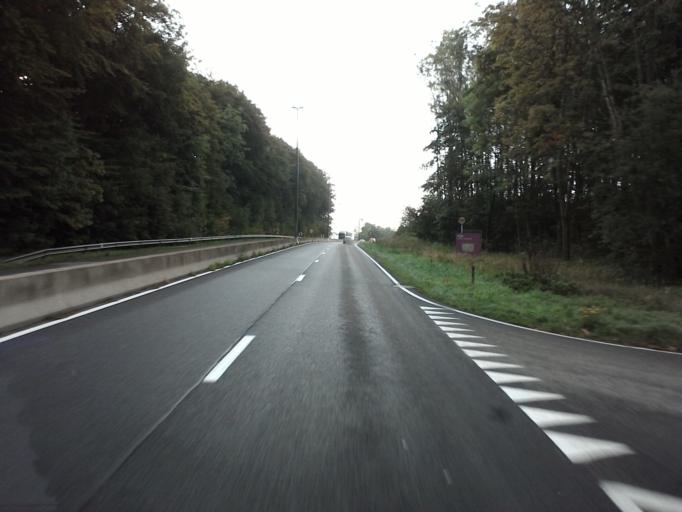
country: BE
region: Wallonia
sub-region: Province du Luxembourg
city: Attert
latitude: 49.7333
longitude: 5.7911
